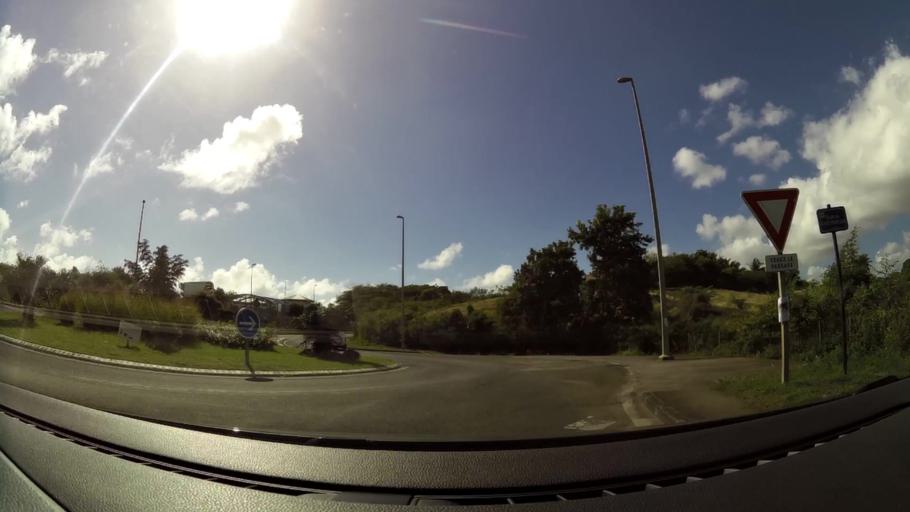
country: GP
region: Guadeloupe
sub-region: Guadeloupe
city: Sainte-Anne
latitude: 16.2488
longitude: -61.3589
